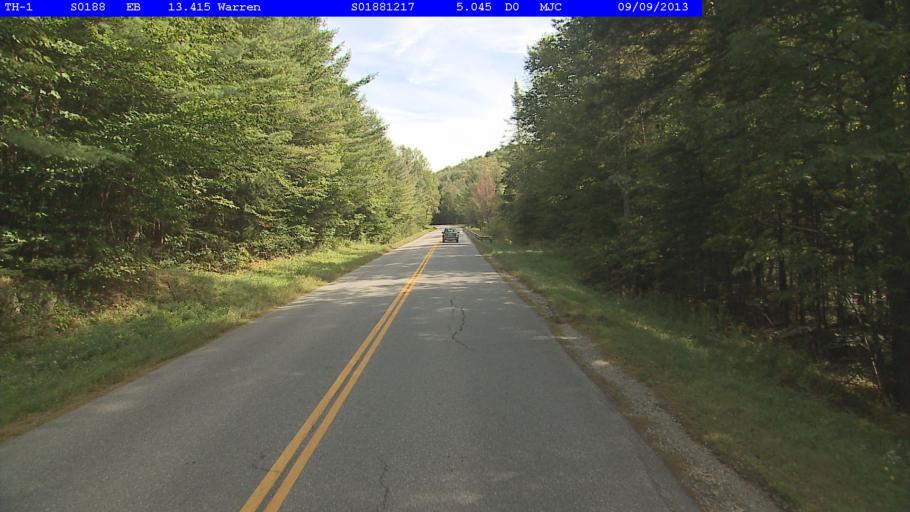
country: US
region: Vermont
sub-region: Washington County
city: Northfield
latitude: 44.1097
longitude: -72.8426
